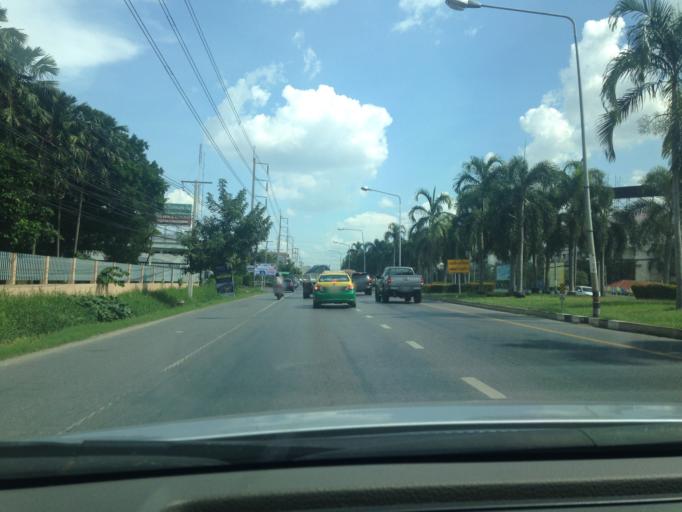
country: TH
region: Phra Nakhon Si Ayutthaya
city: Ban Bang Kadi Pathum Thani
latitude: 13.9932
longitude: 100.5791
